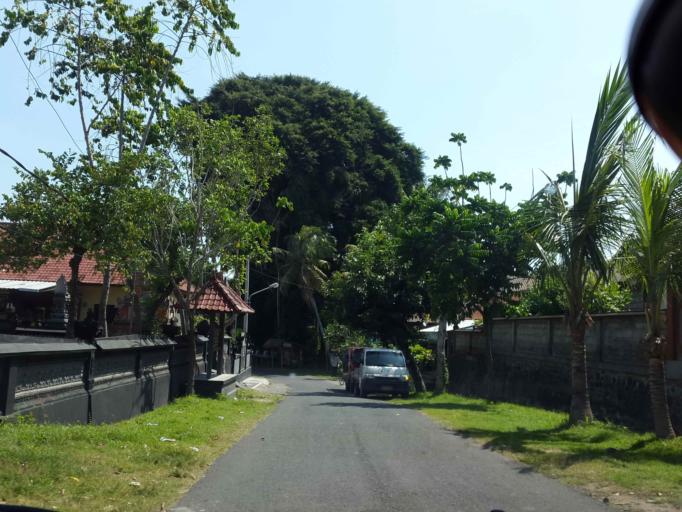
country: ID
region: Bali
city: Klungkung
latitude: -8.5662
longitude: 115.3779
